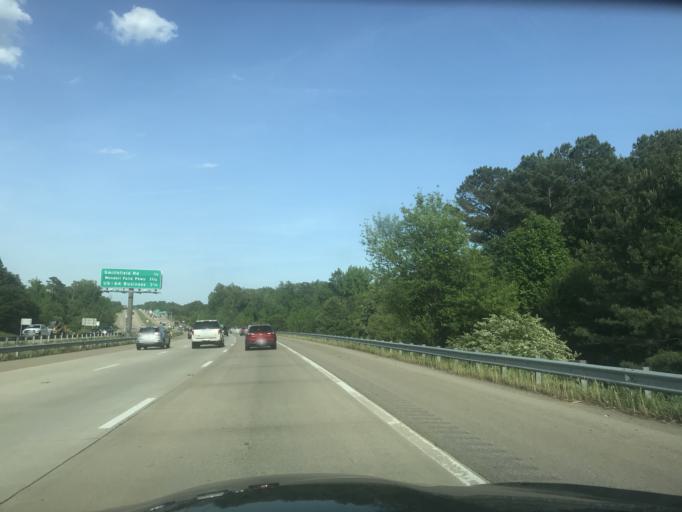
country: US
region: North Carolina
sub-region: Wake County
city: Knightdale
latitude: 35.7651
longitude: -78.4769
